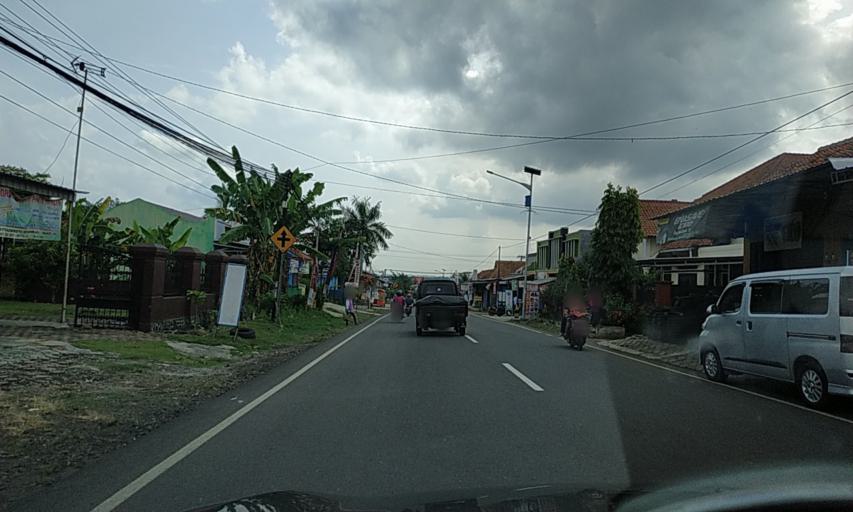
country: ID
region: Central Java
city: Wanareja
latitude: -7.3352
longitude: 108.6846
